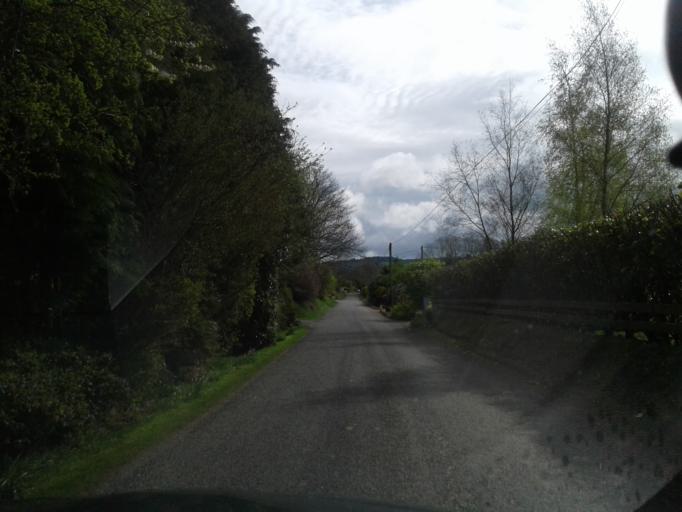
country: IE
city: Newtownmountkennedy
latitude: 53.0905
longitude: -6.2126
